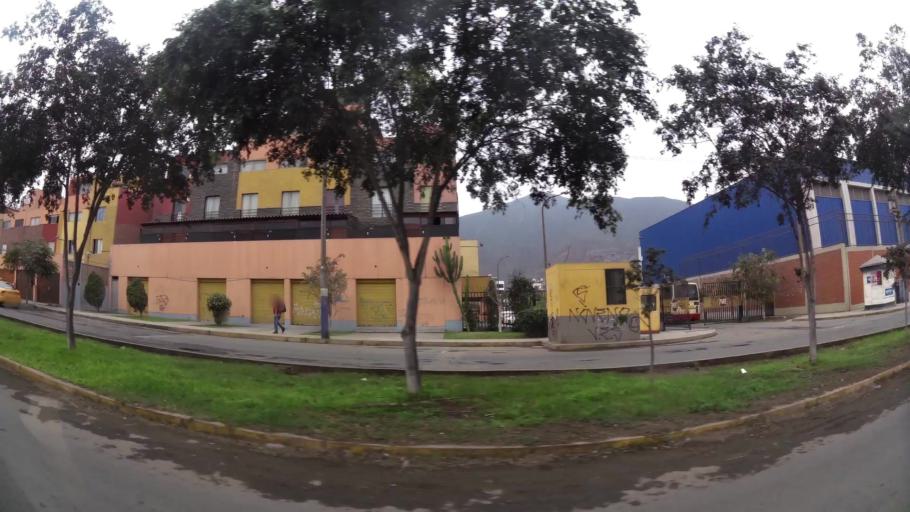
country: PE
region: Lima
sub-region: Lima
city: La Molina
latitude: -12.0621
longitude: -76.9382
